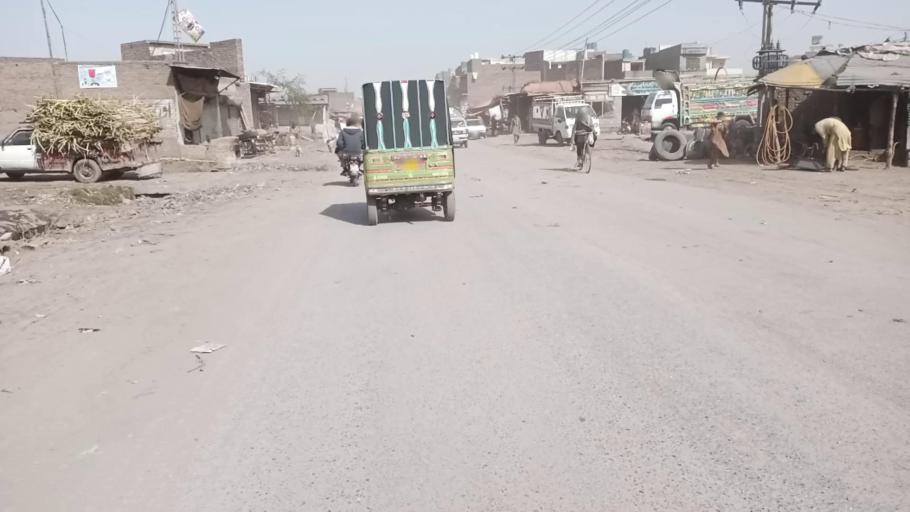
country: PK
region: Khyber Pakhtunkhwa
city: Peshawar
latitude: 33.9908
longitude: 71.6335
